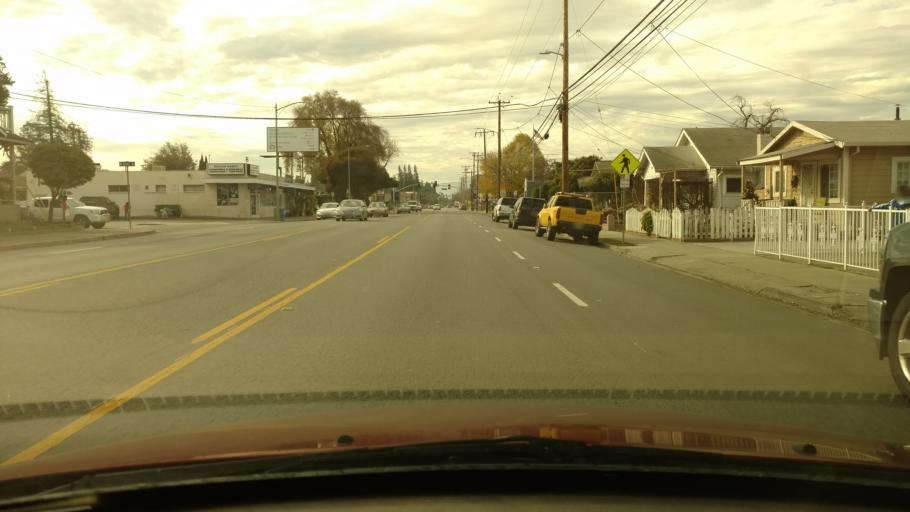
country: US
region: California
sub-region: Santa Clara County
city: San Jose
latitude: 37.3155
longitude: -121.8754
